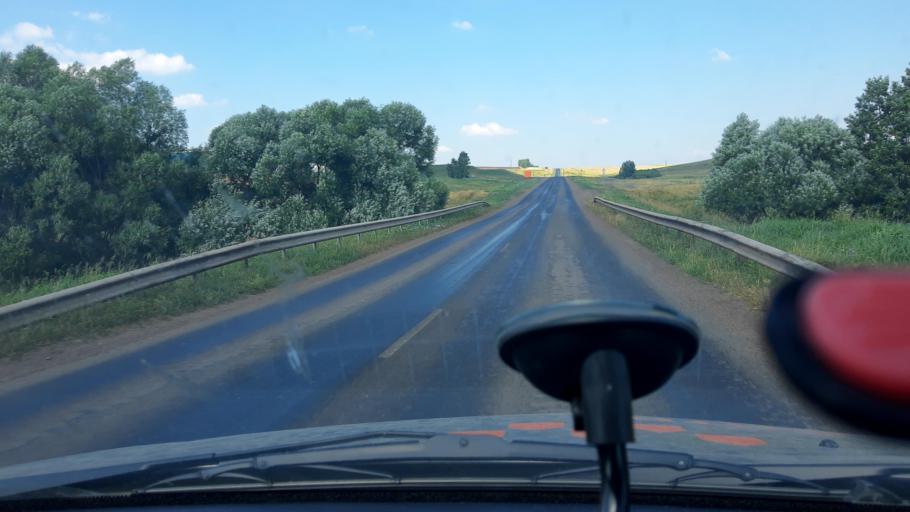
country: RU
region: Bashkortostan
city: Chekmagush
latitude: 55.0612
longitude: 54.6264
